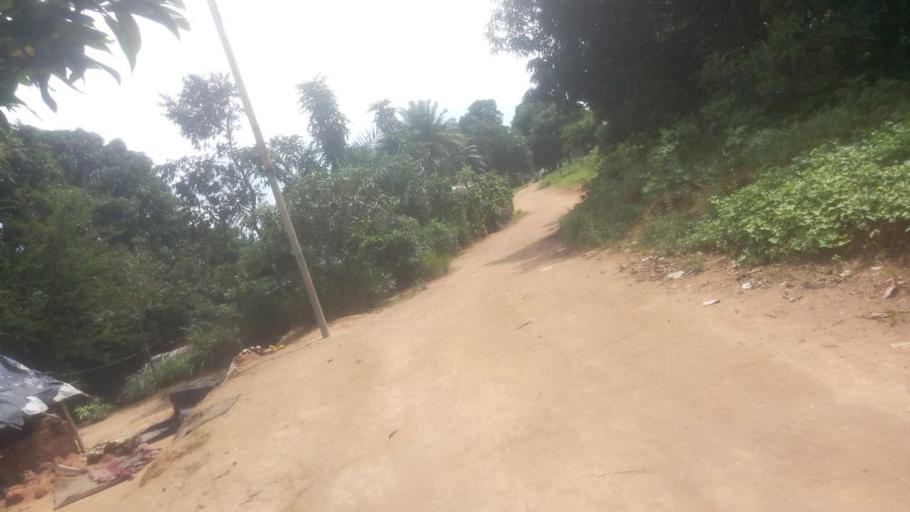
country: SL
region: Northern Province
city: Masoyila
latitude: 8.5295
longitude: -13.1499
